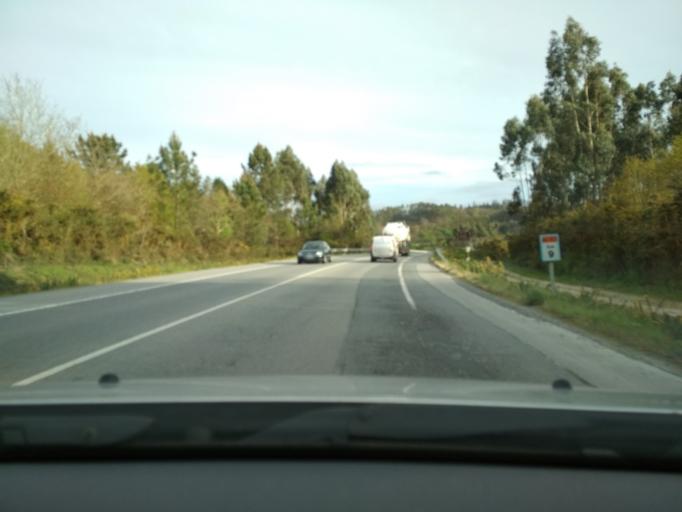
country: ES
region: Galicia
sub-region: Provincia da Coruna
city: Cerceda
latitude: 43.2225
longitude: -8.4587
